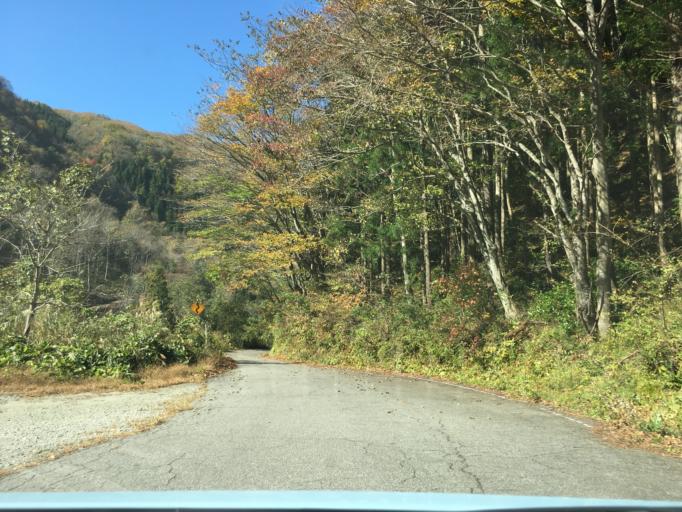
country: JP
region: Fukushima
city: Inawashiro
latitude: 37.3997
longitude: 140.0050
